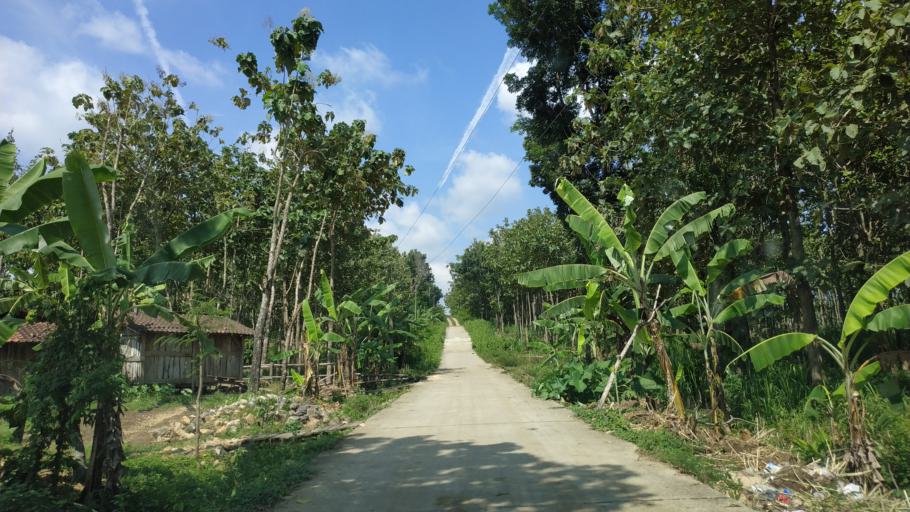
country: ID
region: Central Java
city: Guyangan
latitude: -7.0046
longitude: 111.0931
